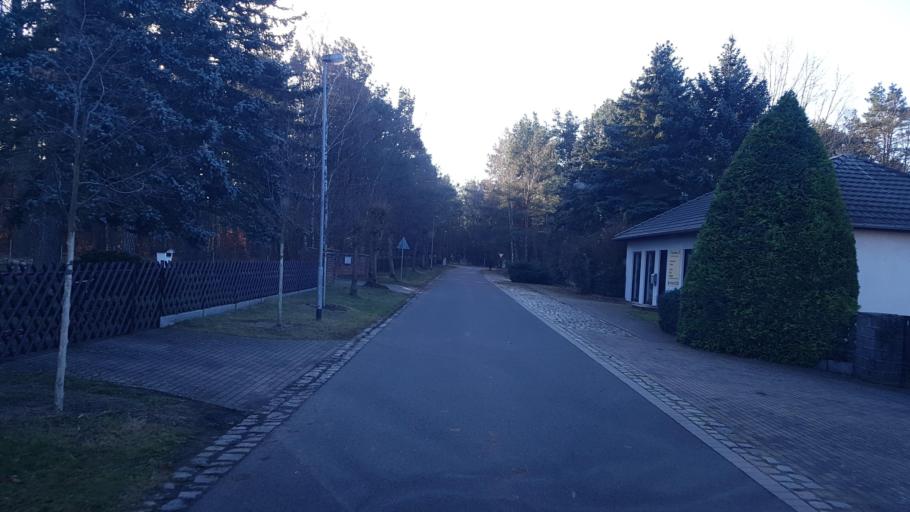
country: DE
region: Brandenburg
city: Heinersbruck
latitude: 51.7429
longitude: 14.5160
